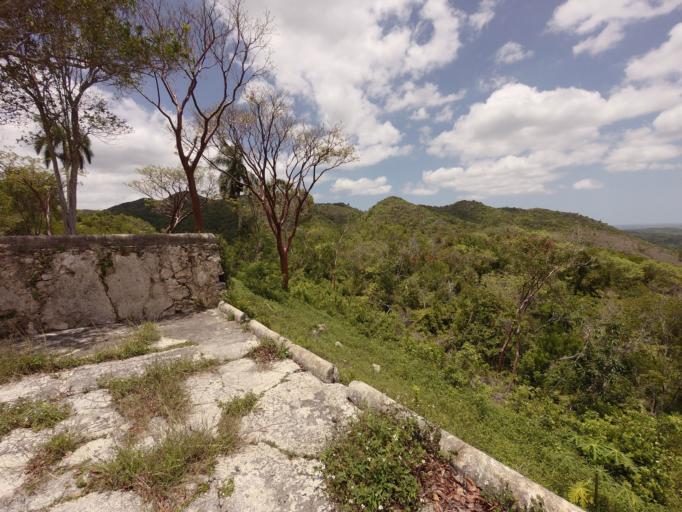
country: CU
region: Artemisa
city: Soroa
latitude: 22.8627
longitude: -82.9282
